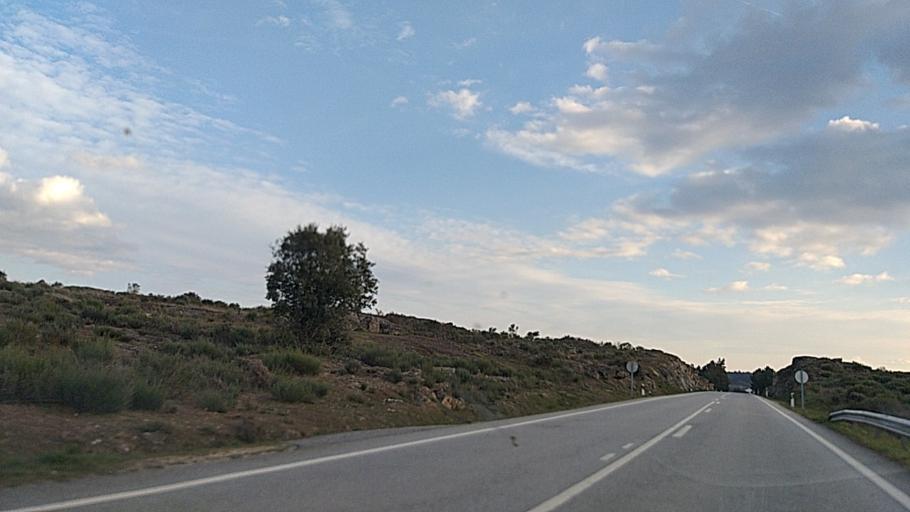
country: PT
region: Guarda
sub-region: Pinhel
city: Pinhel
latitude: 40.6815
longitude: -6.9504
